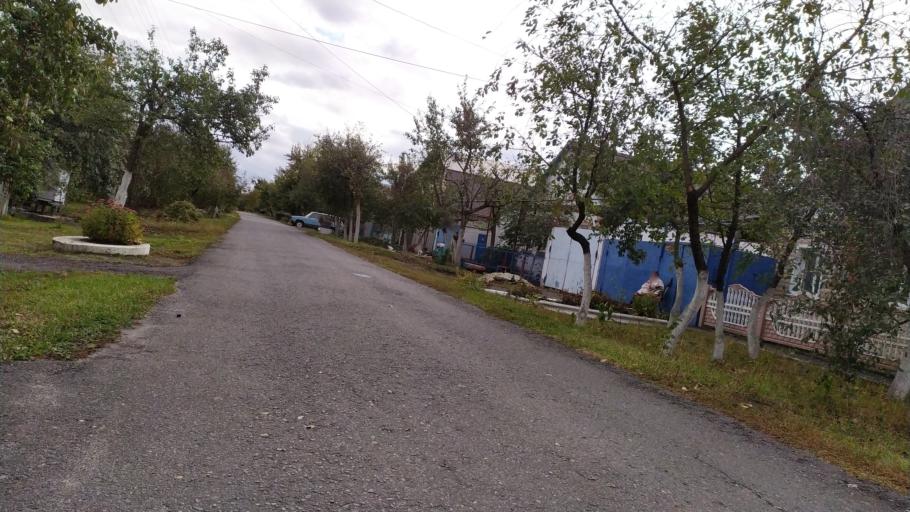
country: RU
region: Kursk
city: Kursk
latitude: 51.6453
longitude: 36.1521
